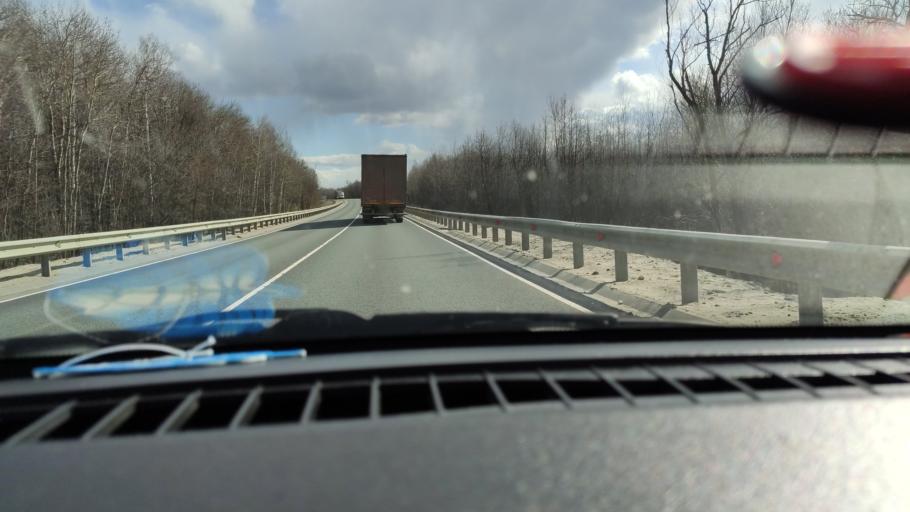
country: RU
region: Saratov
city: Khvalynsk
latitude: 52.4765
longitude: 48.0137
